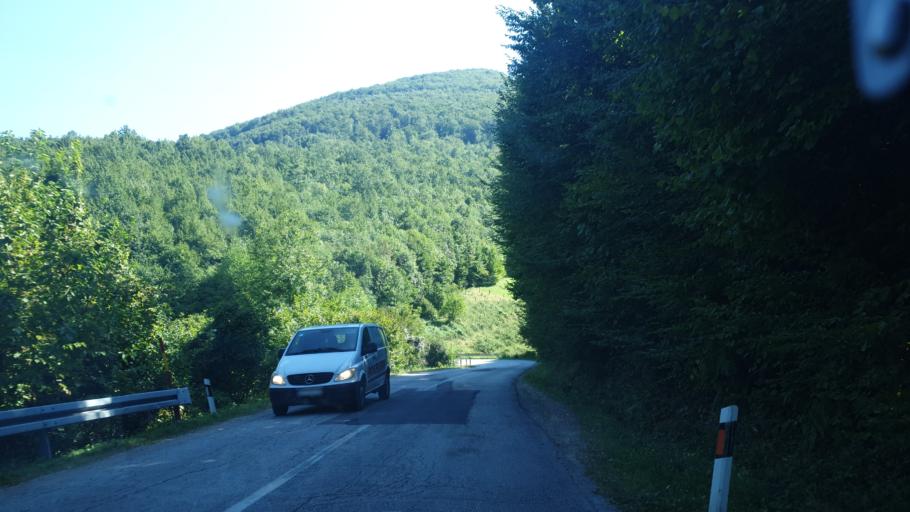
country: RS
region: Central Serbia
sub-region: Kolubarski Okrug
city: Mionica
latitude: 44.1554
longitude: 19.9991
